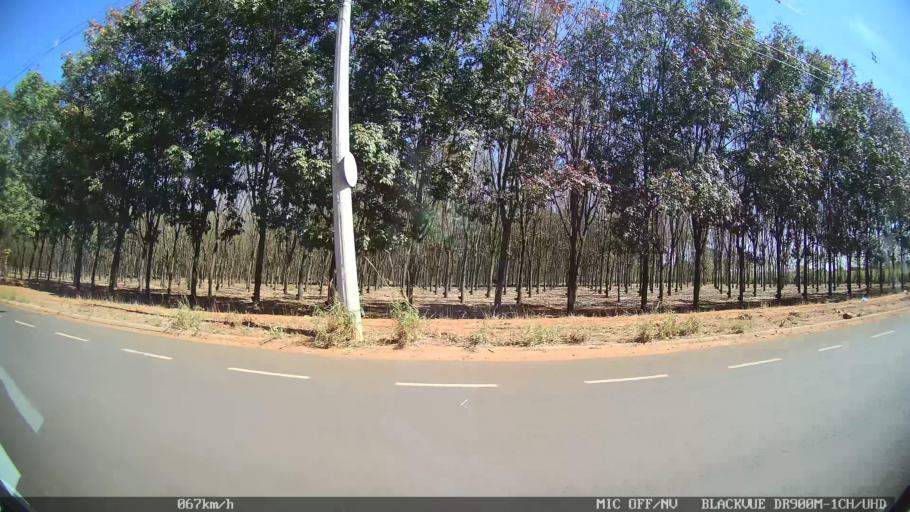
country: BR
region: Sao Paulo
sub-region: Sao Jose Do Rio Preto
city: Sao Jose do Rio Preto
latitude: -20.7351
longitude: -49.4358
